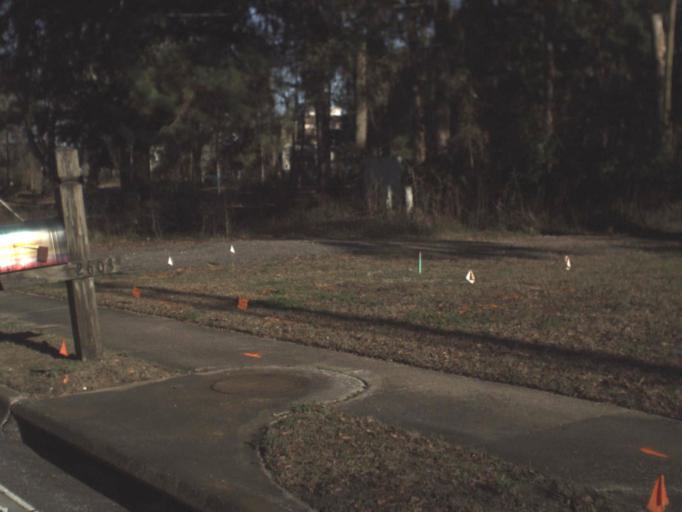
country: US
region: Florida
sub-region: Leon County
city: Tallahassee
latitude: 30.4574
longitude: -84.2352
